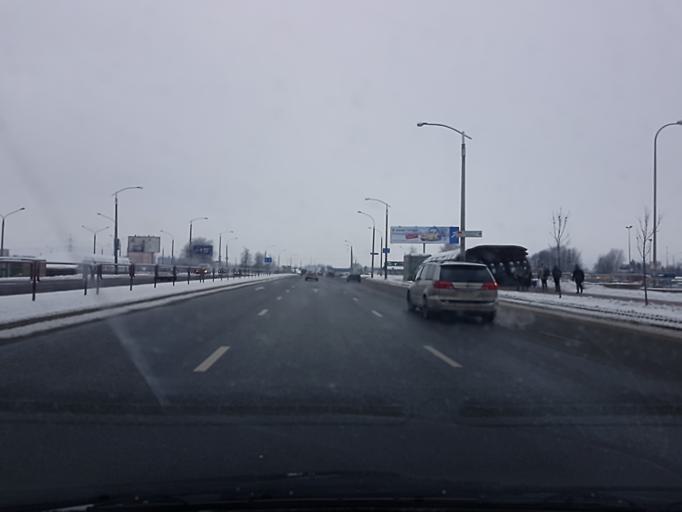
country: BY
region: Minsk
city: Shchomyslitsa
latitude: 53.8468
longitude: 27.4729
